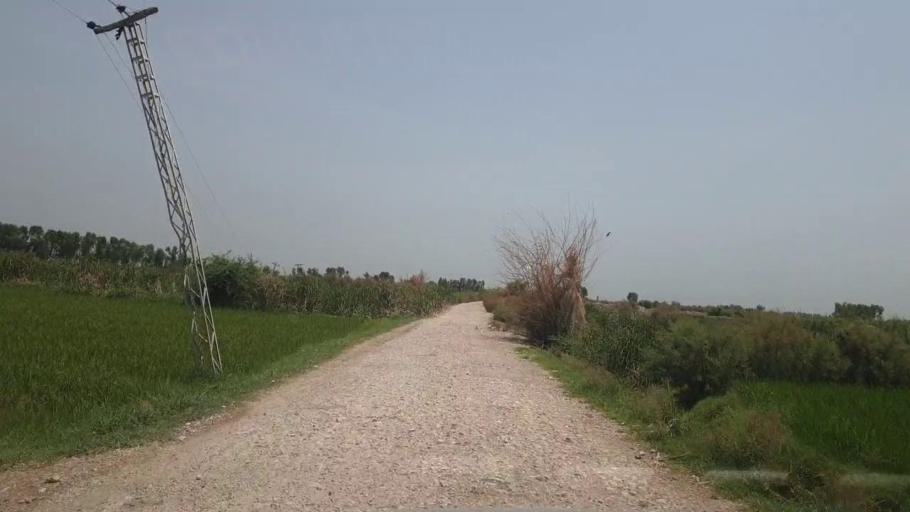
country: PK
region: Sindh
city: Garhi Yasin
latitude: 27.9233
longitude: 68.3774
